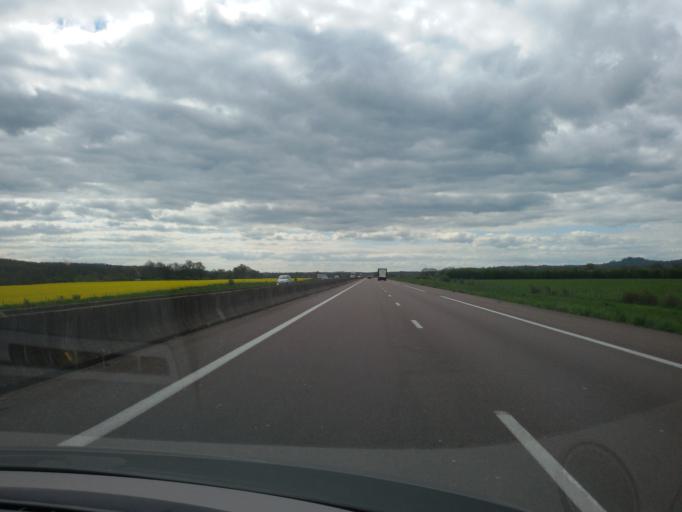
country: FR
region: Bourgogne
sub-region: Departement de la Cote-d'Or
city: Pouilly-en-Auxois
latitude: 47.2908
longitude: 4.5066
